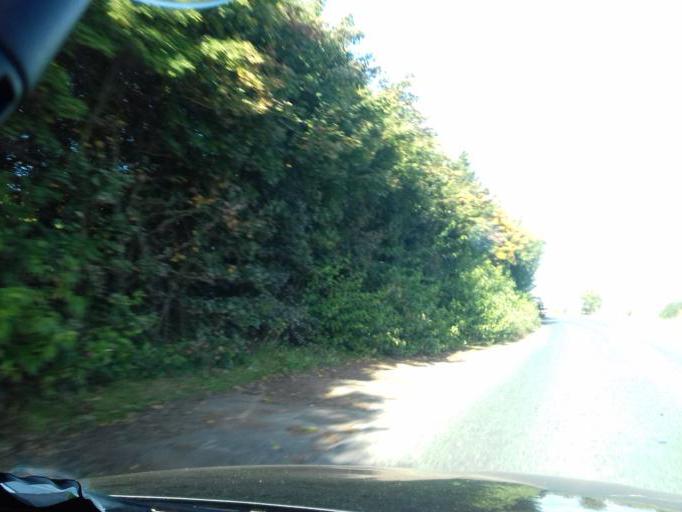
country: IE
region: Leinster
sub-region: Fingal County
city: Swords
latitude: 53.4347
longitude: -6.2298
